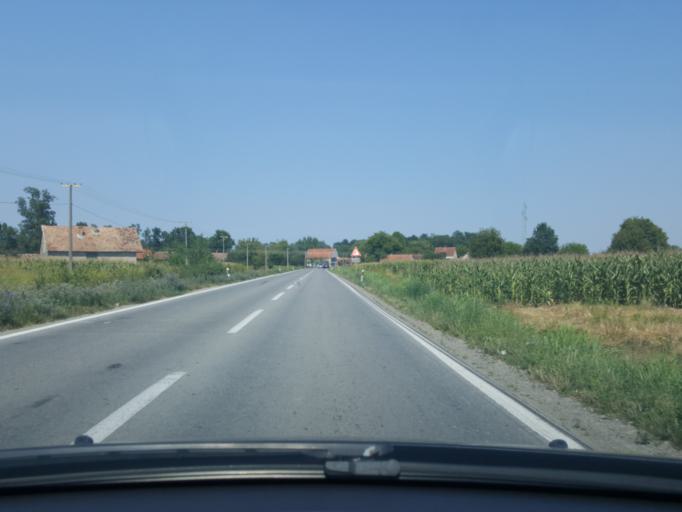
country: RS
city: Stitar
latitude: 44.7662
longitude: 19.5896
